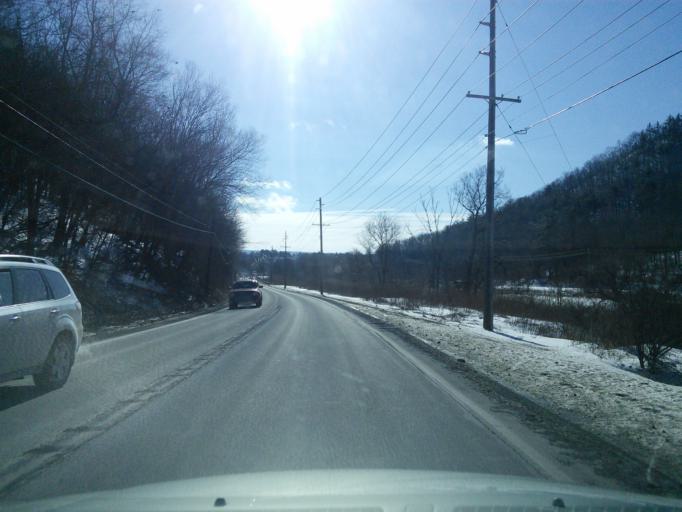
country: US
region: Pennsylvania
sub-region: Centre County
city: Milesburg
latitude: 40.9311
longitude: -77.7844
